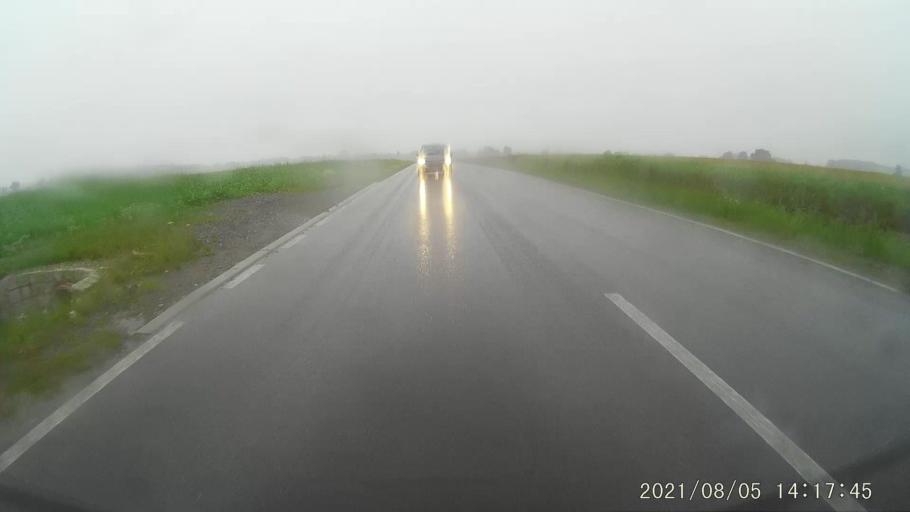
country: PL
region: Opole Voivodeship
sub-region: Powiat prudnicki
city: Biala
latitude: 50.4625
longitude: 17.7013
